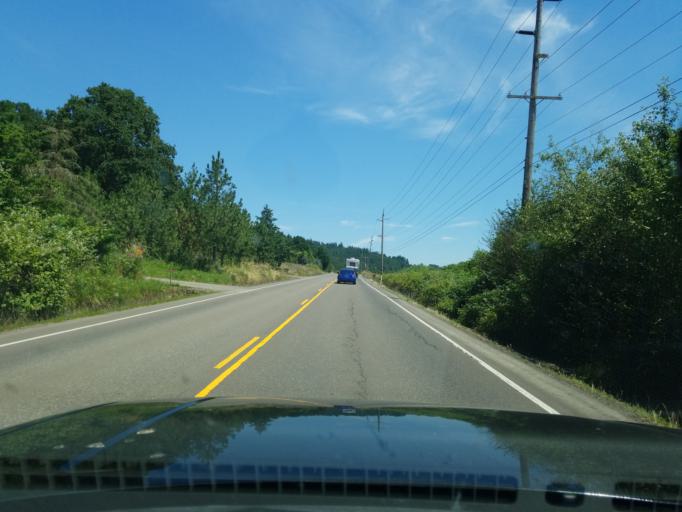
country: US
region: Oregon
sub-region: Yamhill County
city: Yamhill
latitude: 45.3671
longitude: -123.1640
